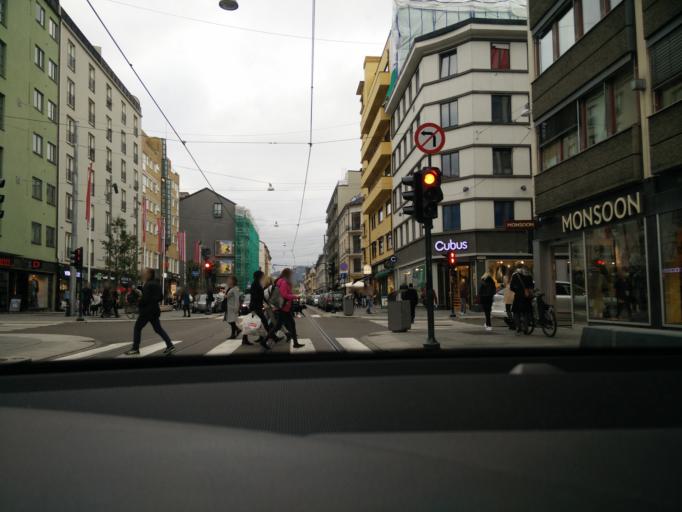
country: NO
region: Oslo
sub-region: Oslo
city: Oslo
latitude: 59.9264
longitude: 10.7215
